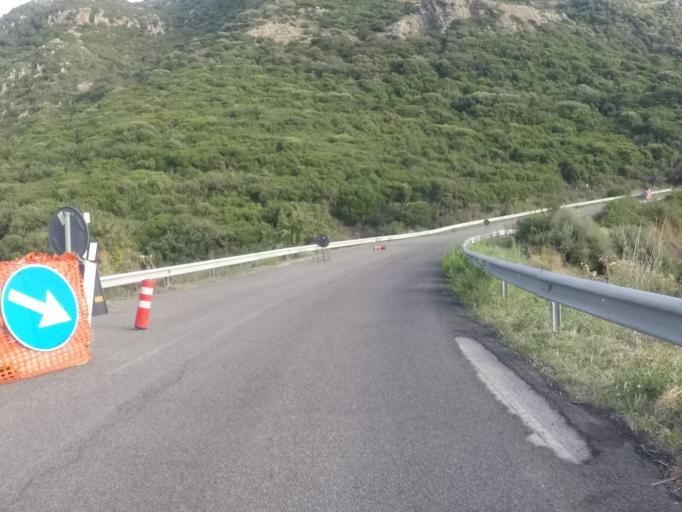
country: IT
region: Sardinia
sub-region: Provincia di Oristano
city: Montresta
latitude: 40.4067
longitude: 8.4133
